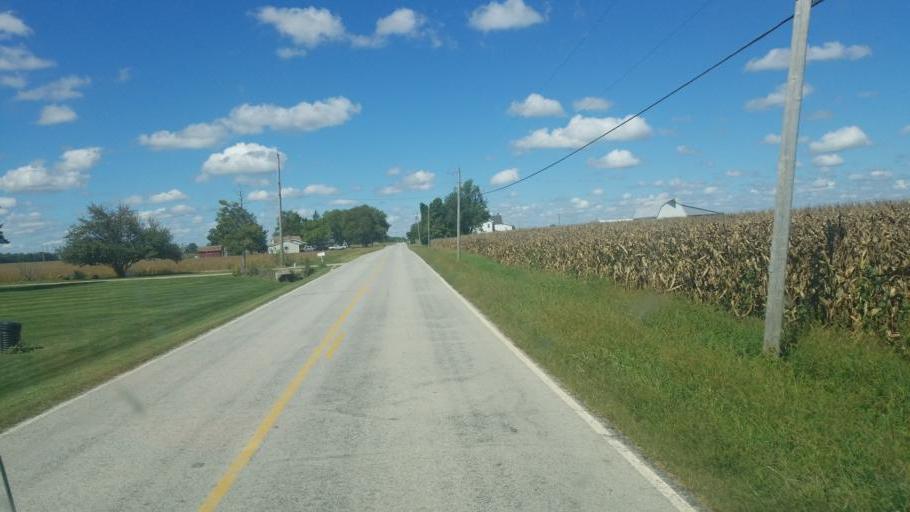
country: US
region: Ohio
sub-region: Madison County
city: West Jefferson
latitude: 39.9956
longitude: -83.2901
